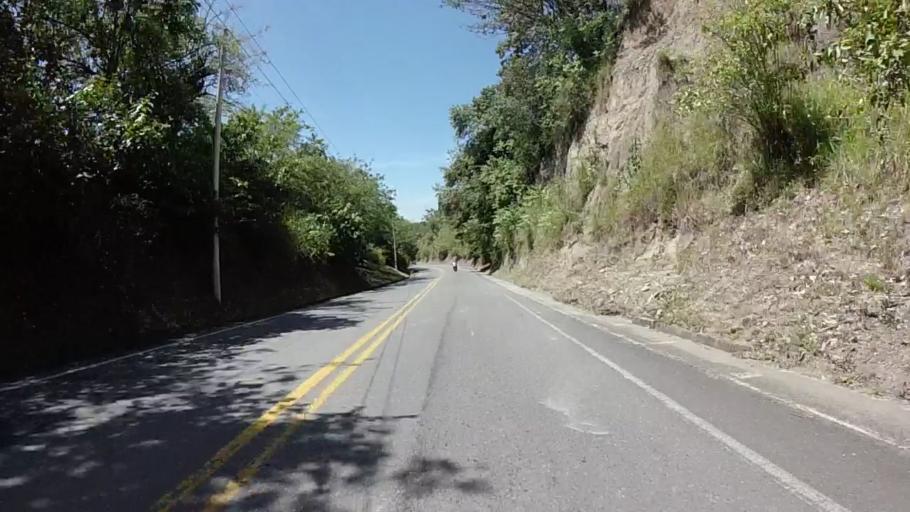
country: CO
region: Valle del Cauca
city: Cartago
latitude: 4.7350
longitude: -75.8964
